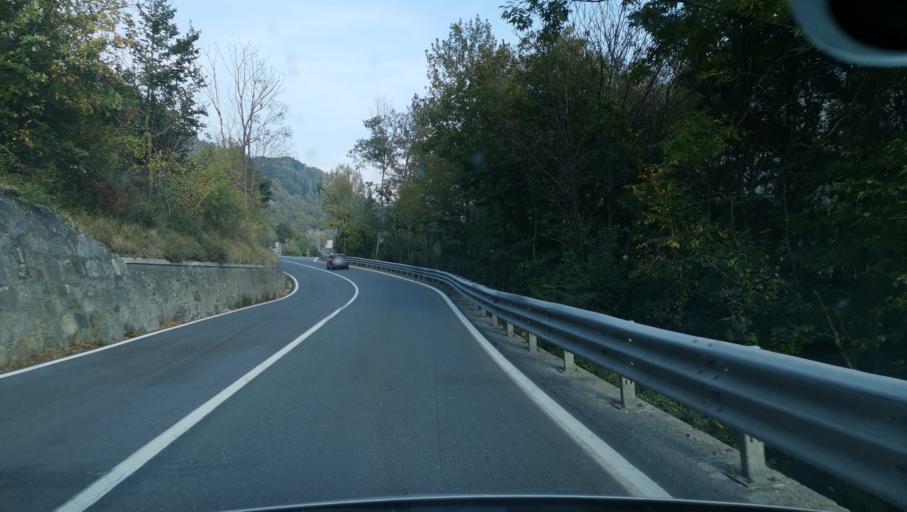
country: IT
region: Piedmont
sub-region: Provincia di Torino
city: Salbertrand
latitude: 45.0769
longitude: 6.8902
